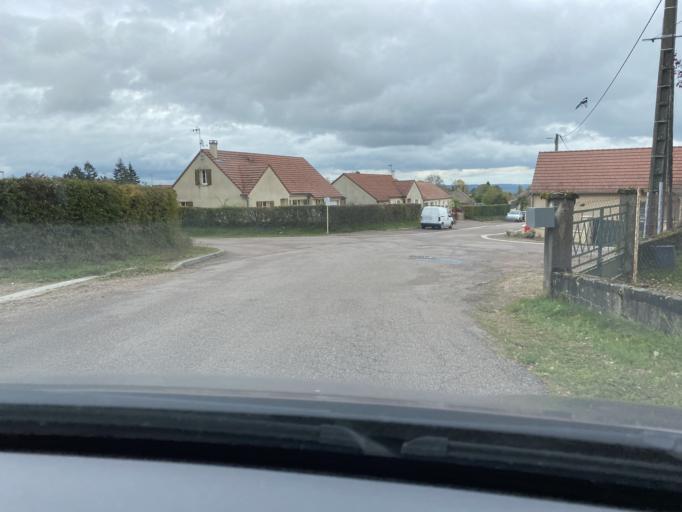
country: FR
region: Bourgogne
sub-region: Departement de la Cote-d'Or
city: Saulieu
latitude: 47.2839
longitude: 4.2232
